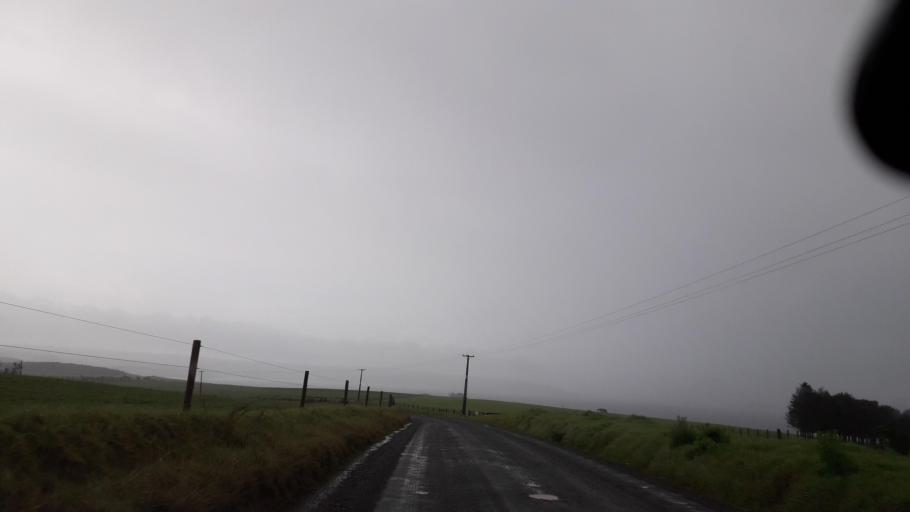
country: NZ
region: Northland
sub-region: Far North District
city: Kerikeri
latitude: -35.1294
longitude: 174.0107
